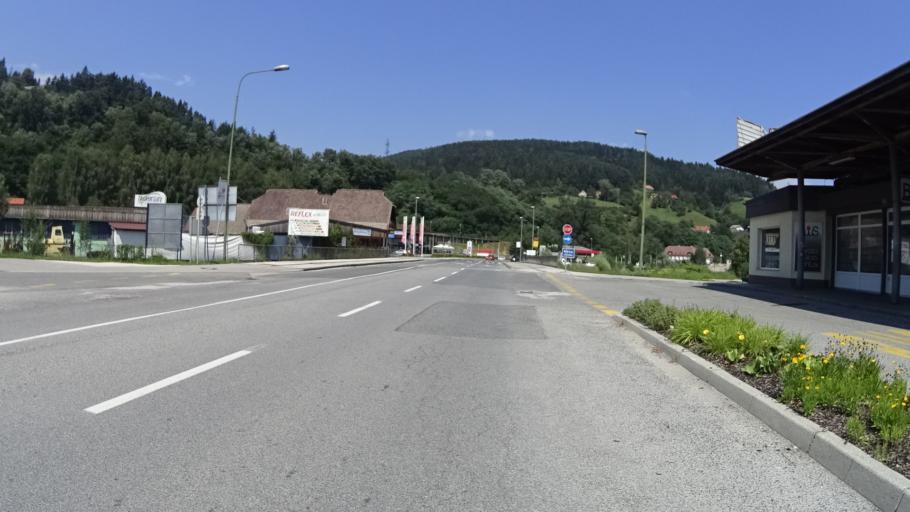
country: SI
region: Ravne na Koroskem
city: Ravne na Koroskem
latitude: 46.5454
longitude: 14.9630
